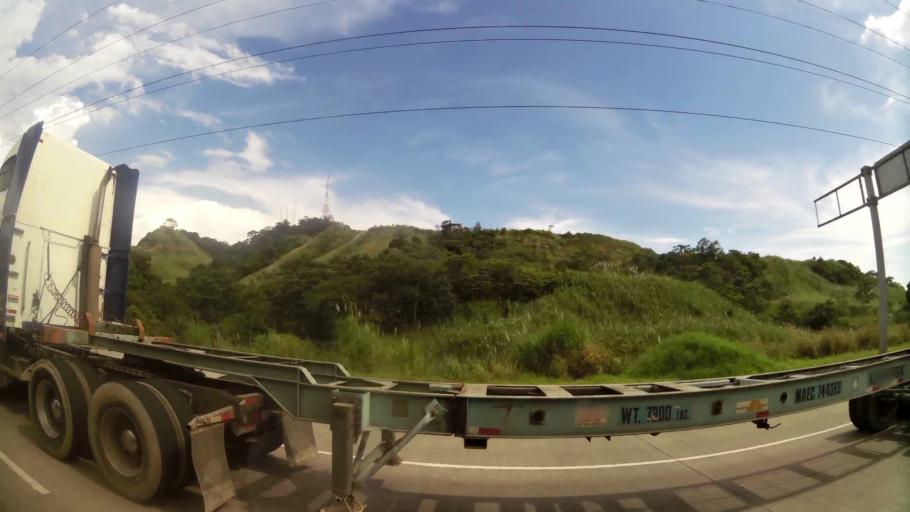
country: PA
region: Panama
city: Las Cumbres
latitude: 9.0509
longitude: -79.5267
